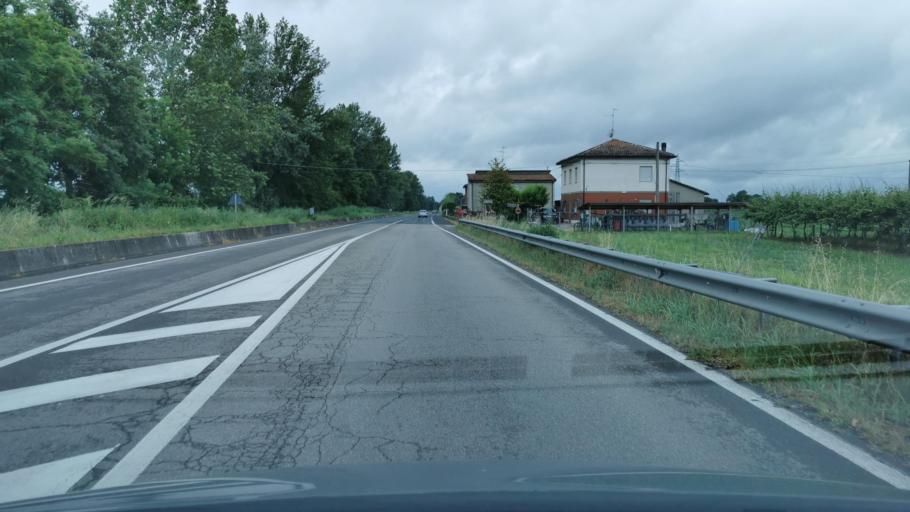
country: IT
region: Emilia-Romagna
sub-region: Provincia di Ravenna
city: Cotignola
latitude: 44.3778
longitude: 11.9483
